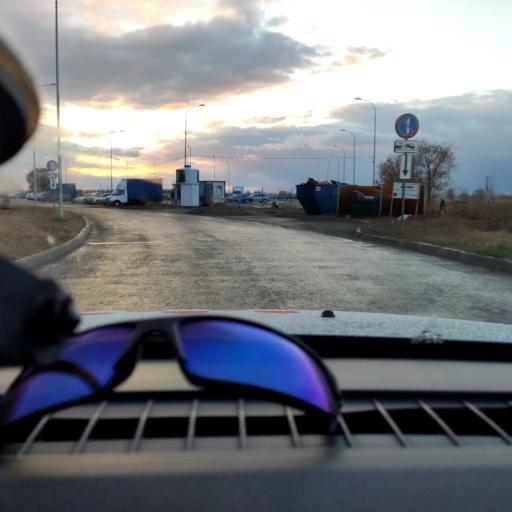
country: RU
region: Samara
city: Samara
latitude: 53.1190
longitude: 50.1579
